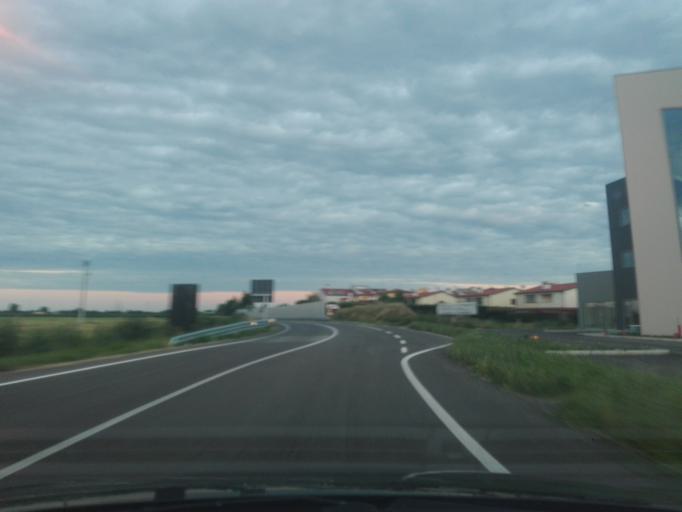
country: IT
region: Veneto
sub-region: Provincia di Rovigo
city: Santa Maria Maddalena
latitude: 44.9068
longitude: 11.6073
